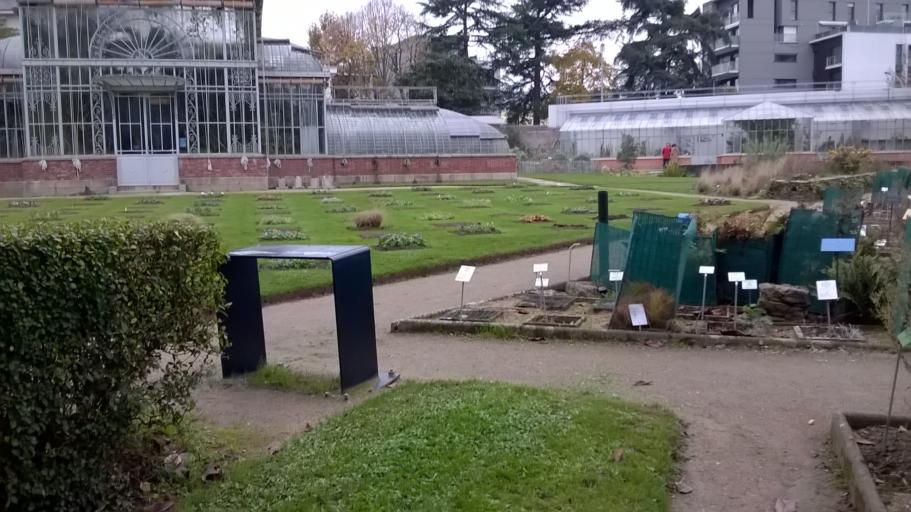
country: FR
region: Pays de la Loire
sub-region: Departement de la Loire-Atlantique
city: Nantes
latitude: 47.2207
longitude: -1.5432
